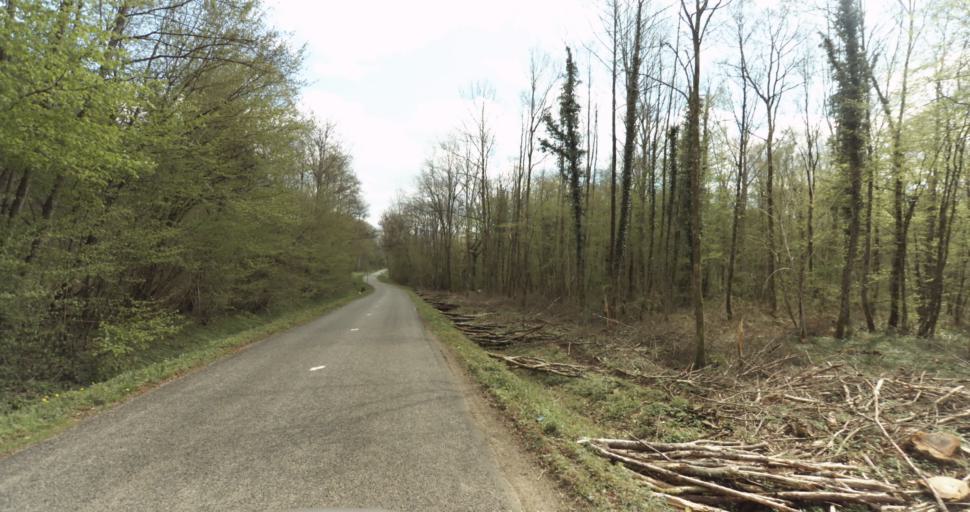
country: FR
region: Franche-Comte
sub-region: Departement du Jura
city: Champvans
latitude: 47.1644
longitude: 5.4503
